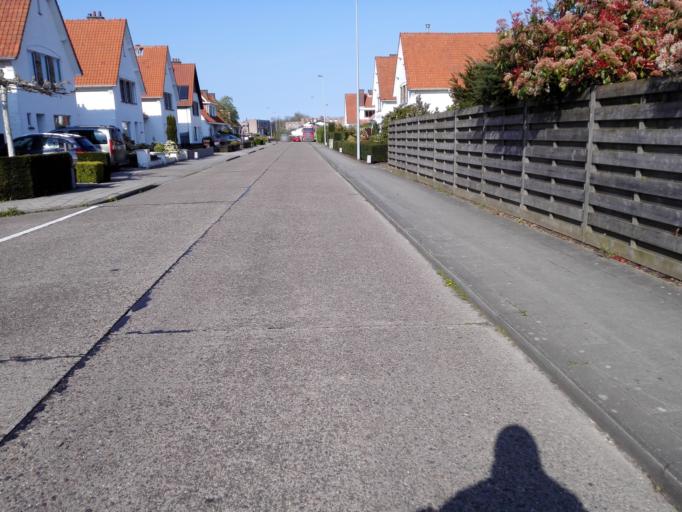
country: BE
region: Flanders
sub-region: Provincie Vlaams-Brabant
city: Leuven
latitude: 50.8791
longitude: 4.7329
